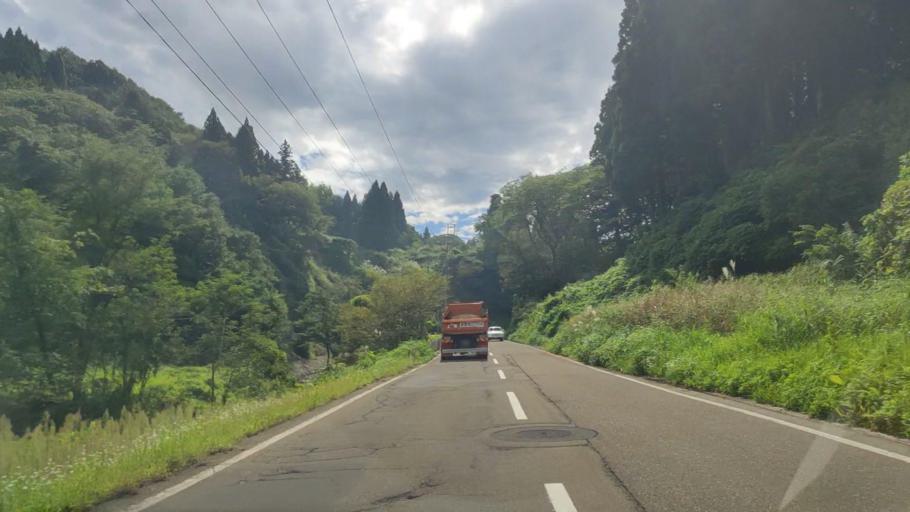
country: JP
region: Niigata
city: Arai
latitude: 36.9429
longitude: 138.2910
